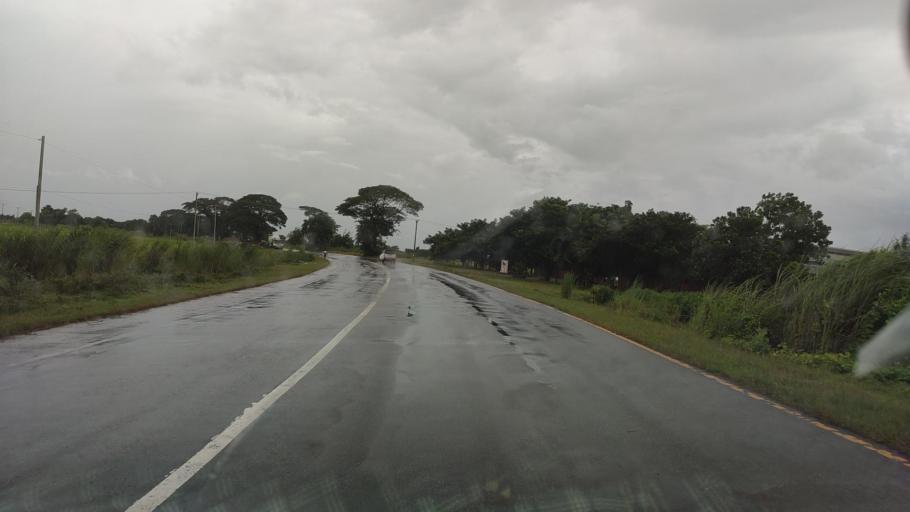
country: MM
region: Bago
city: Nyaunglebin
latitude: 17.7200
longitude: 96.5991
